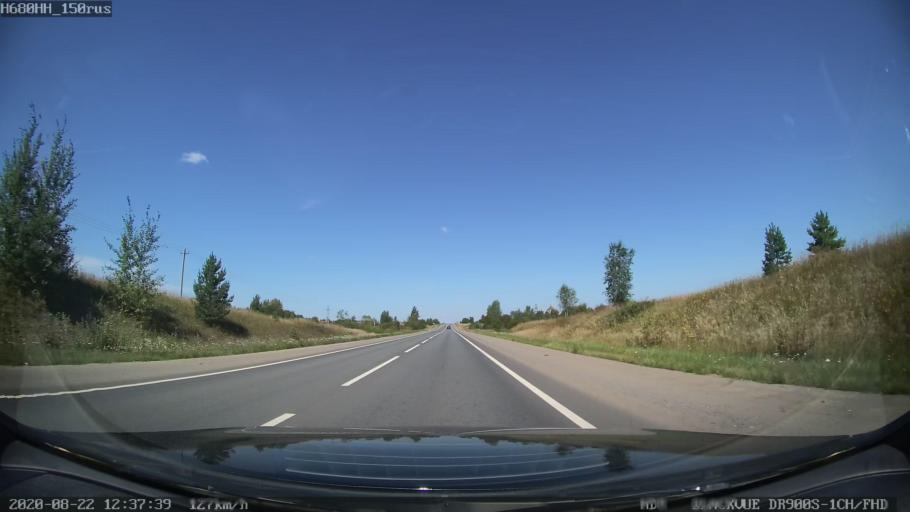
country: RU
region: Tverskaya
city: Rameshki
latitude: 57.2997
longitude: 36.0889
